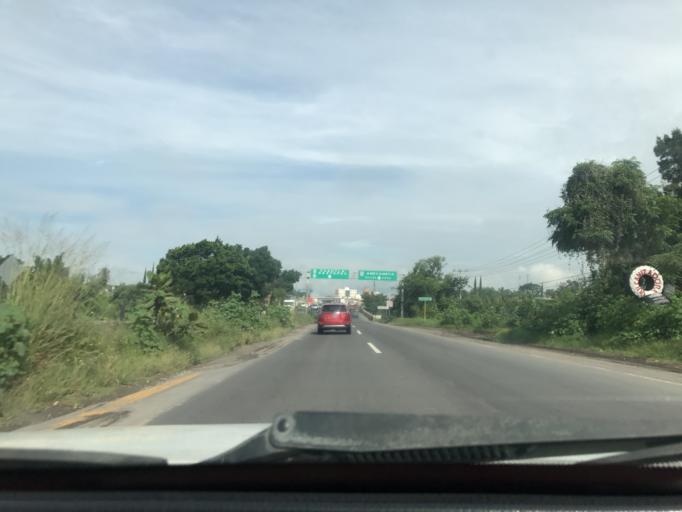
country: MX
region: Morelos
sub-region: Cuautla
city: Tierra Larga (Campo Nuevo)
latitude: 18.8468
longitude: -98.9314
